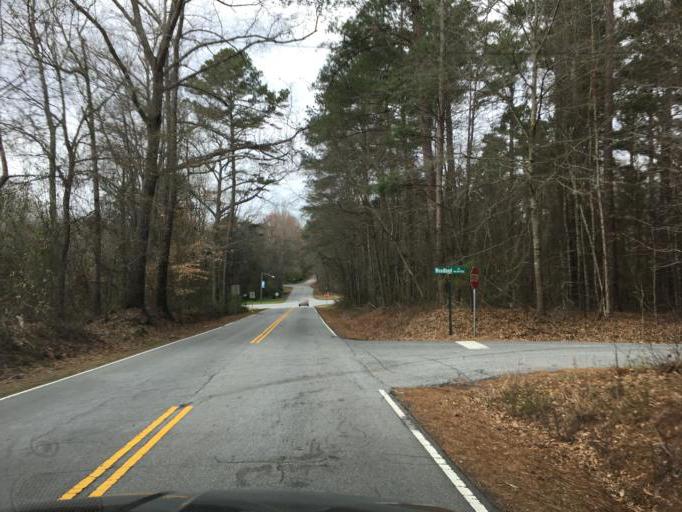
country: US
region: South Carolina
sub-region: Anderson County
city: Pendleton
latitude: 34.6600
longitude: -82.7893
